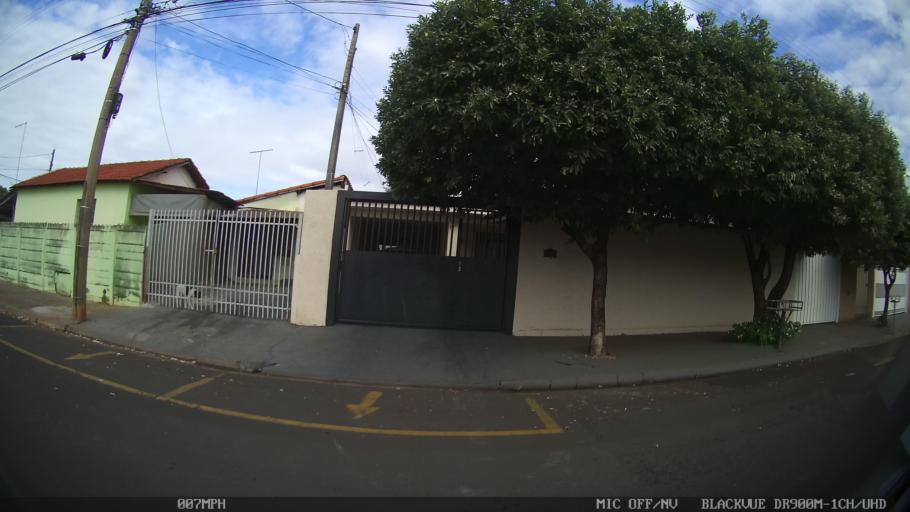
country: BR
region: Sao Paulo
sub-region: Sao Jose Do Rio Preto
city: Sao Jose do Rio Preto
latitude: -20.8366
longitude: -49.3756
